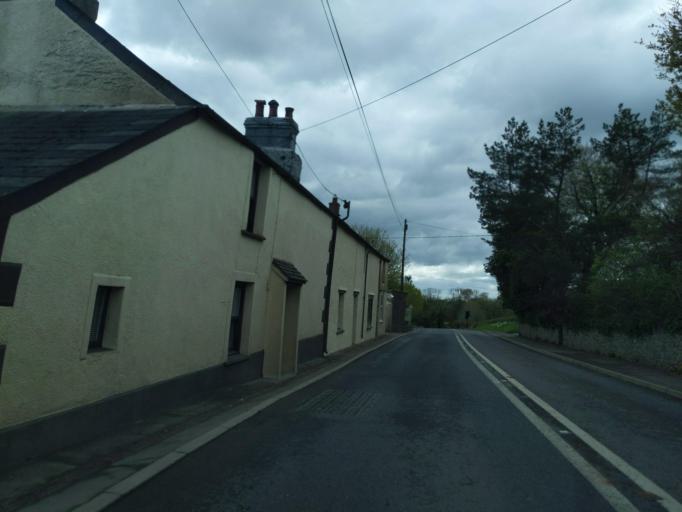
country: GB
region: England
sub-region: Cornwall
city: Pensilva
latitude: 50.4817
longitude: -4.3759
